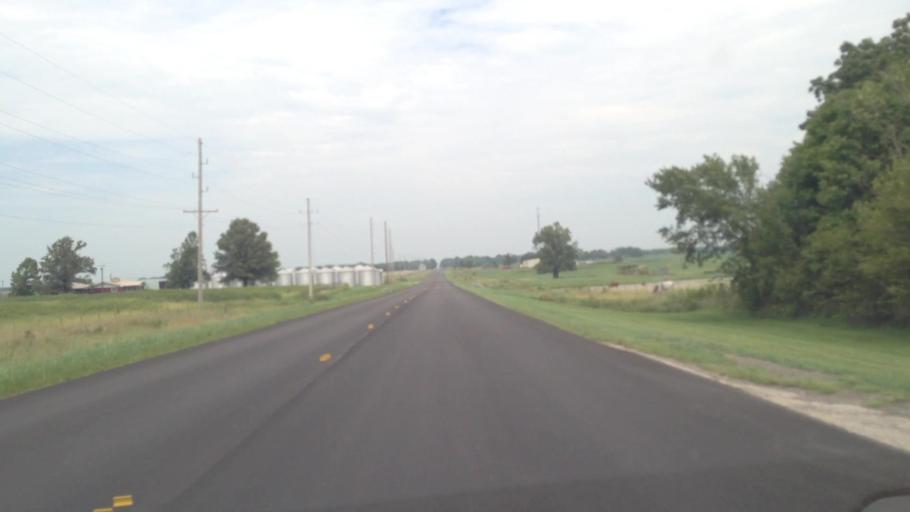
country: US
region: Kansas
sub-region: Allen County
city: Iola
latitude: 37.8935
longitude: -95.1701
